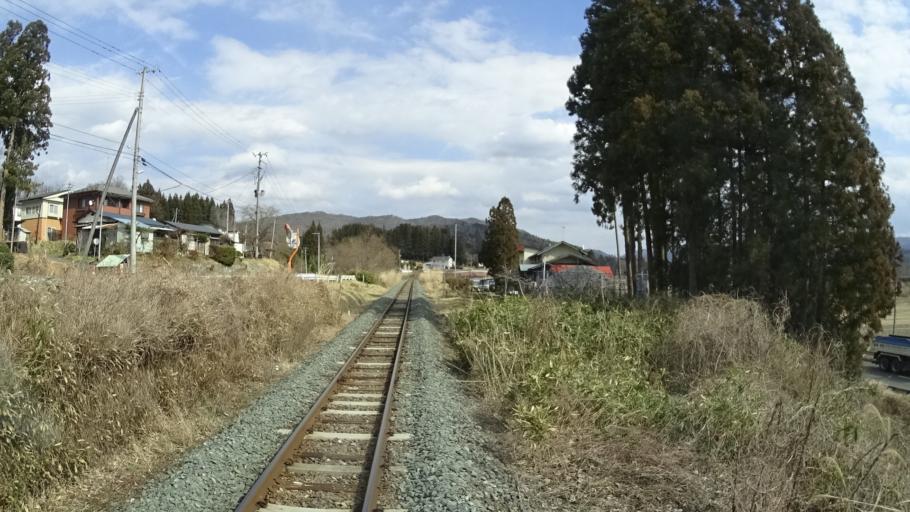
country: JP
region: Iwate
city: Hanamaki
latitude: 39.3778
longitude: 141.2462
